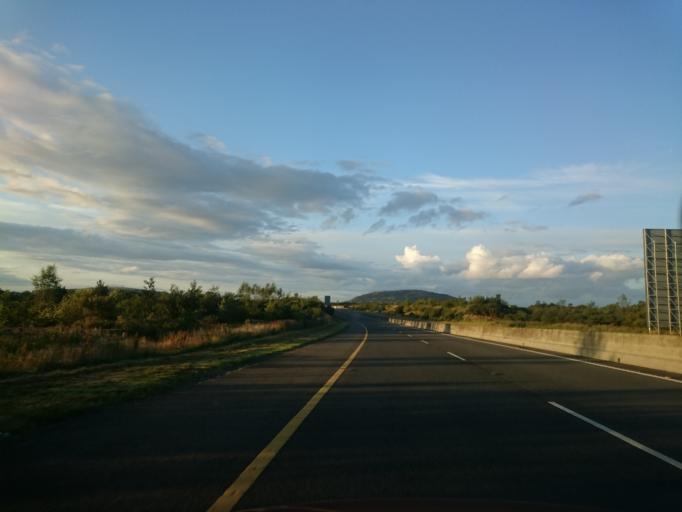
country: IE
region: Leinster
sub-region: Loch Garman
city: Gorey
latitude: 52.6688
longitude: -6.2615
